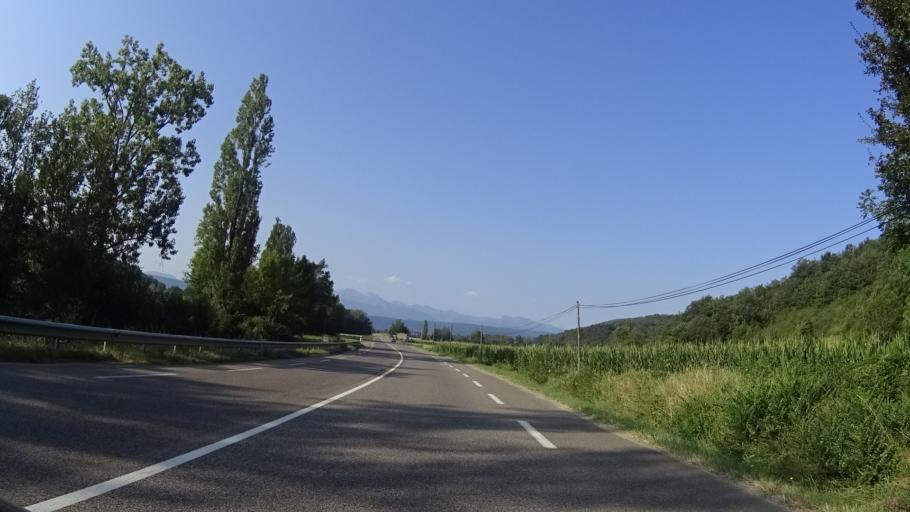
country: FR
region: Midi-Pyrenees
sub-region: Departement de l'Ariege
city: Mirepoix
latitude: 43.0123
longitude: 1.8879
